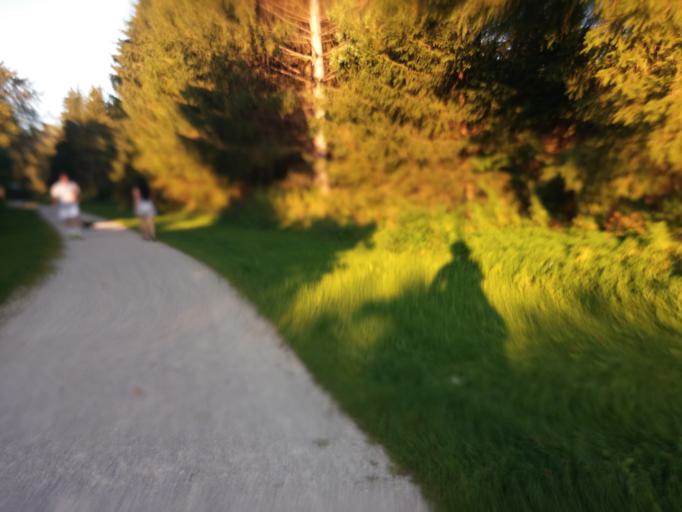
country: DE
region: Bavaria
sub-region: Upper Bavaria
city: Haar
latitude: 48.1005
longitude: 11.7043
